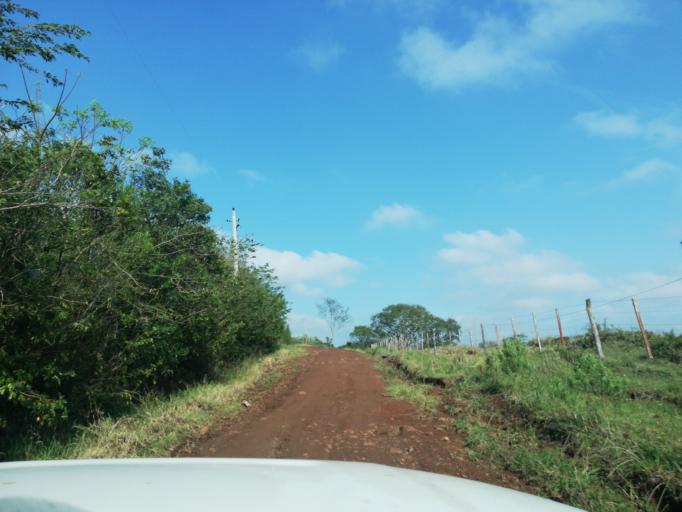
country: AR
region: Misiones
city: Cerro Azul
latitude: -27.5960
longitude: -55.5222
